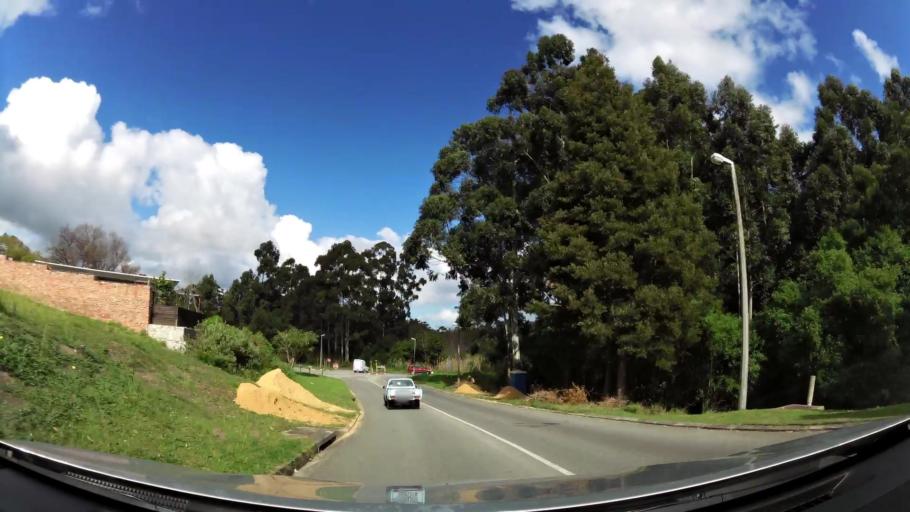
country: ZA
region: Western Cape
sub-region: Eden District Municipality
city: Knysna
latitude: -34.0539
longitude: 23.0761
